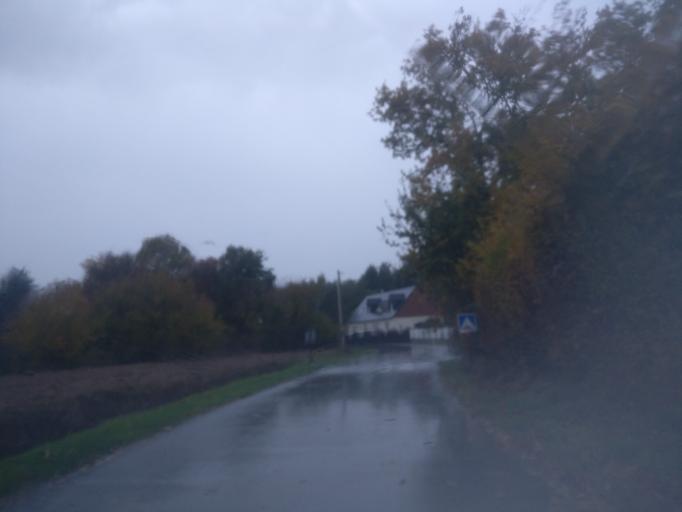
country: FR
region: Brittany
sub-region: Departement d'Ille-et-Vilaine
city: Bruz
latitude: 48.0219
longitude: -1.7647
